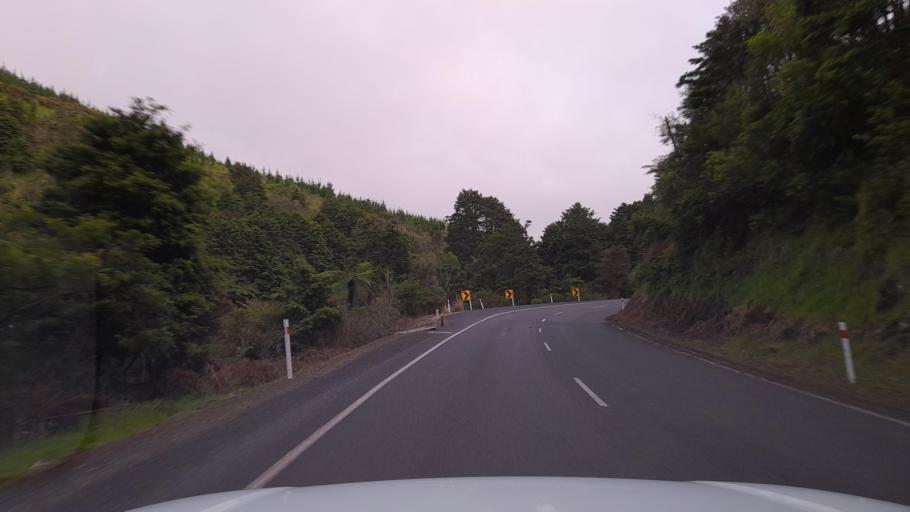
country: NZ
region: Northland
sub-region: Far North District
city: Moerewa
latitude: -35.6106
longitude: 173.8427
